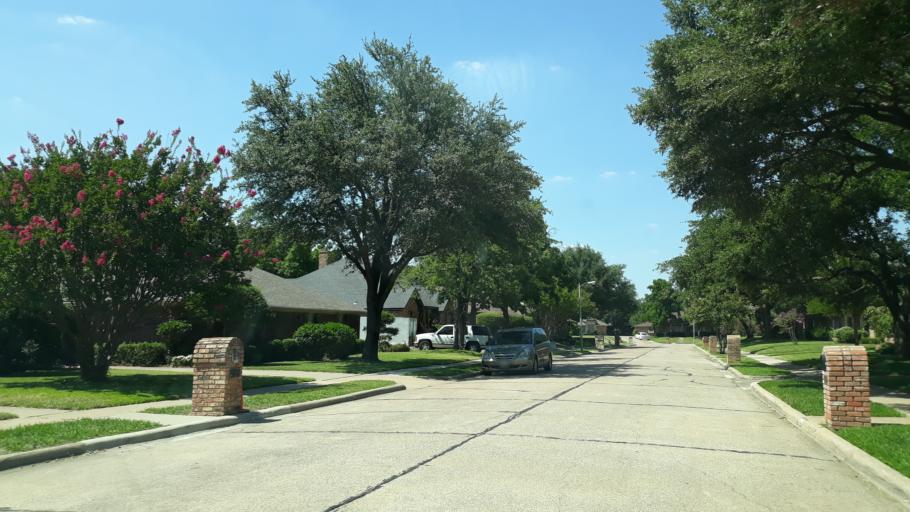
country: US
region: Texas
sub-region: Dallas County
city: Irving
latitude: 32.8281
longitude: -97.0060
